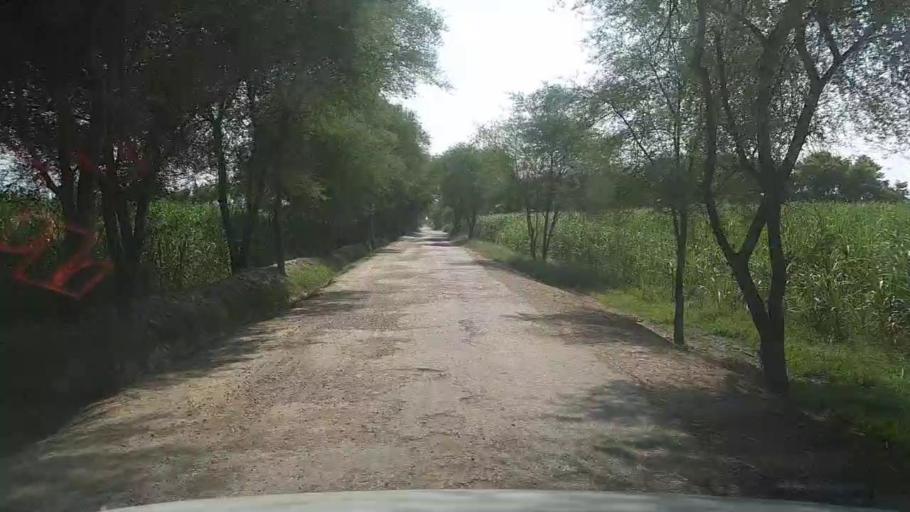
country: PK
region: Sindh
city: Mirpur Mathelo
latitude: 28.1214
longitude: 69.6024
